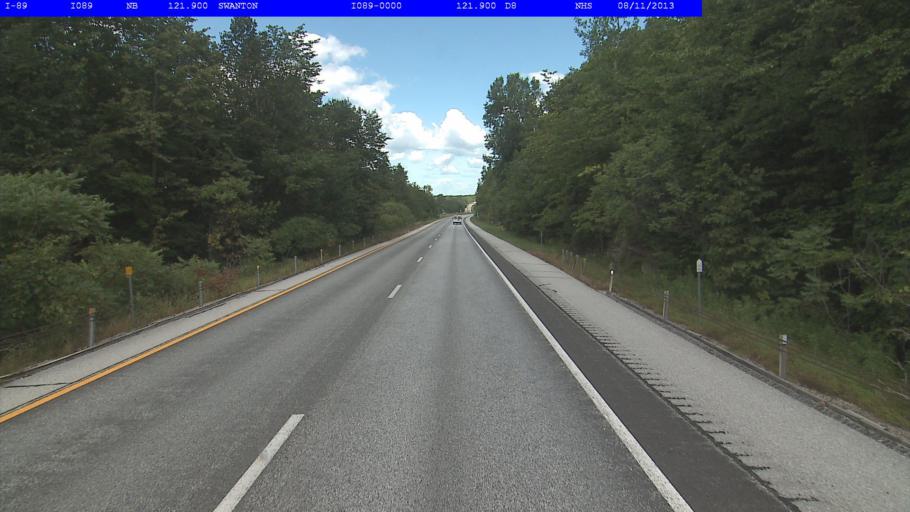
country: US
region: Vermont
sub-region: Franklin County
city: Swanton
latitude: 44.9028
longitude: -73.0954
